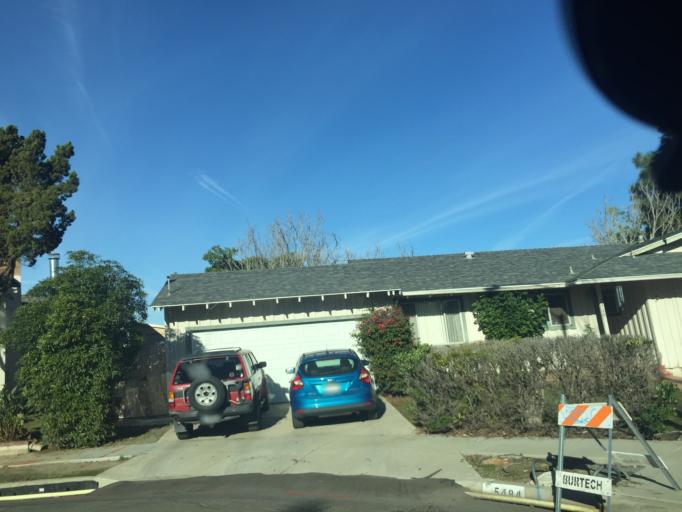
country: US
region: California
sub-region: San Diego County
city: La Mesa
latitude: 32.7775
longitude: -117.0800
